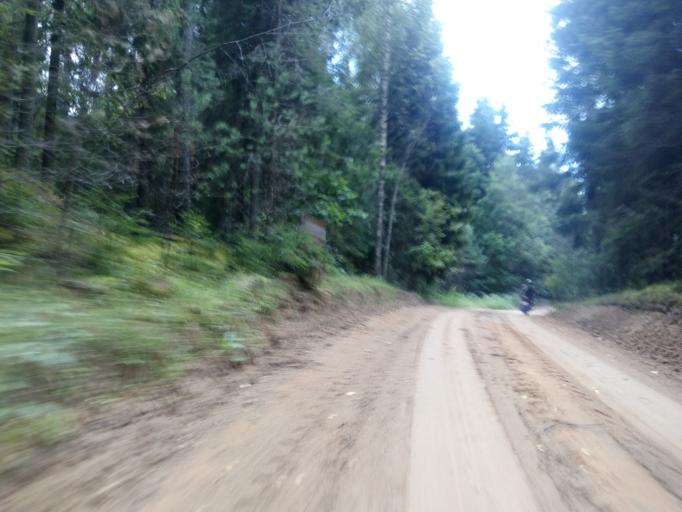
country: BY
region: Vitebsk
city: Dzisna
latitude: 55.6985
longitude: 28.3540
